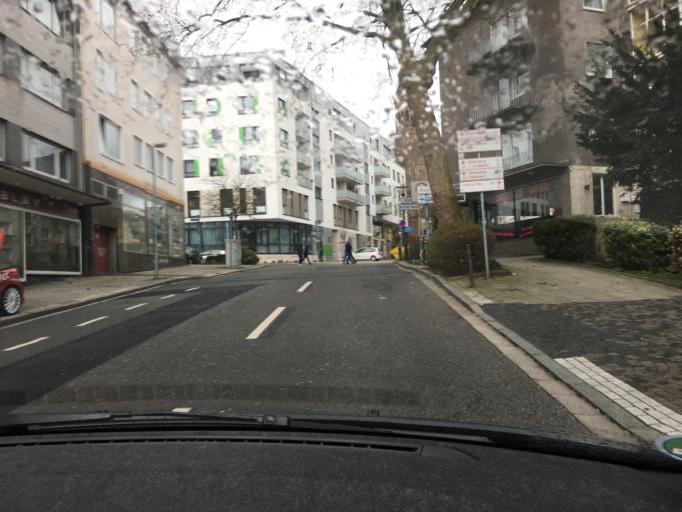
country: DE
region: North Rhine-Westphalia
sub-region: Regierungsbezirk Dusseldorf
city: Essen
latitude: 51.4609
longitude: 7.0106
